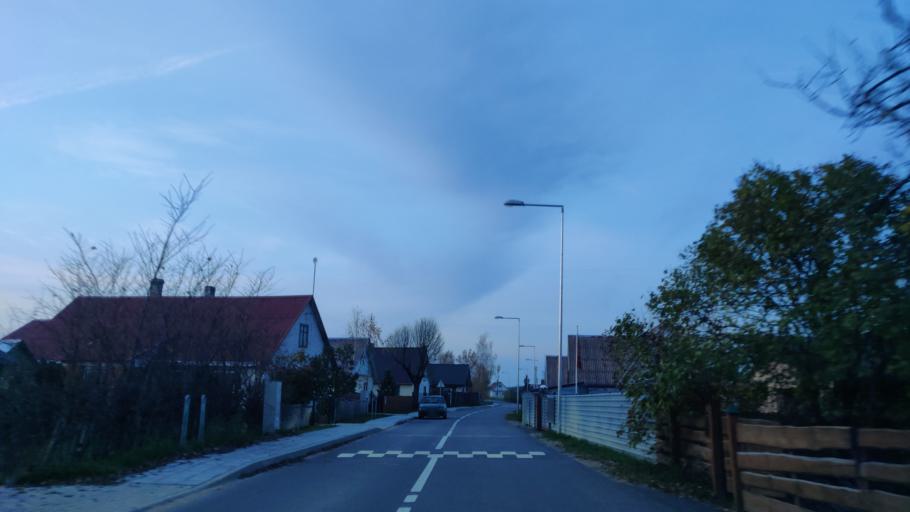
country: LT
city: Lentvaris
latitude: 54.5867
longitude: 25.0512
